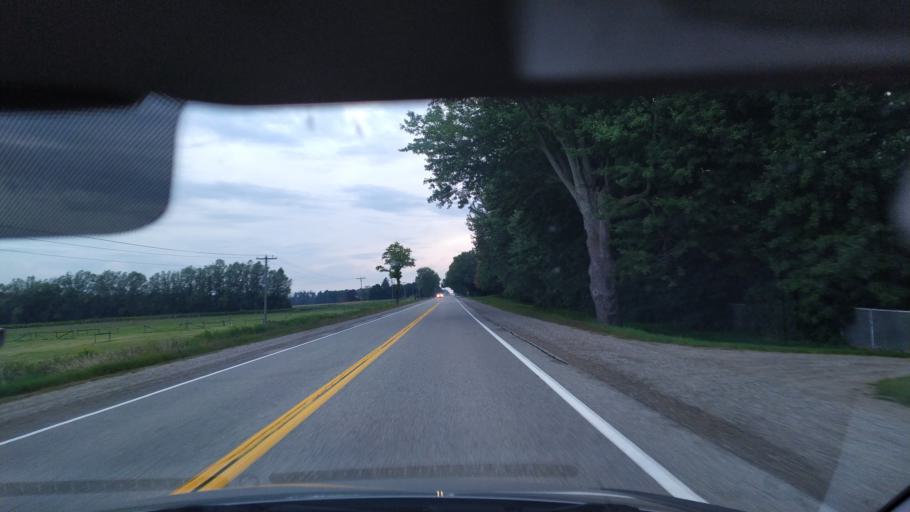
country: CA
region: Ontario
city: Kitchener
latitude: 43.3162
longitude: -80.5395
